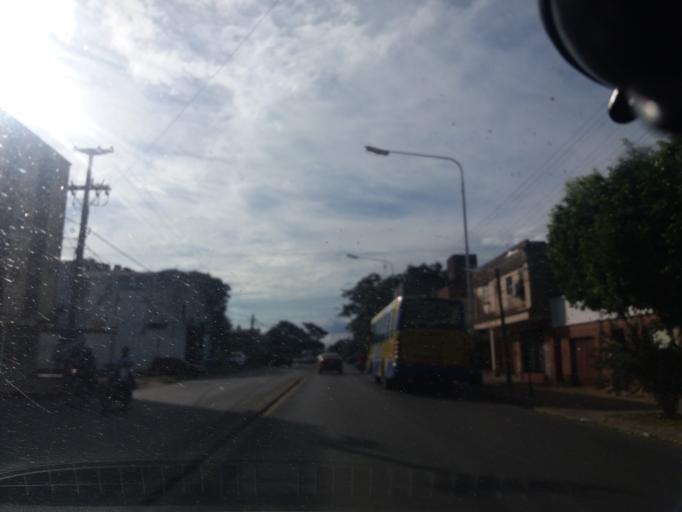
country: AR
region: Corrientes
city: Corrientes
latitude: -27.4858
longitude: -58.8236
